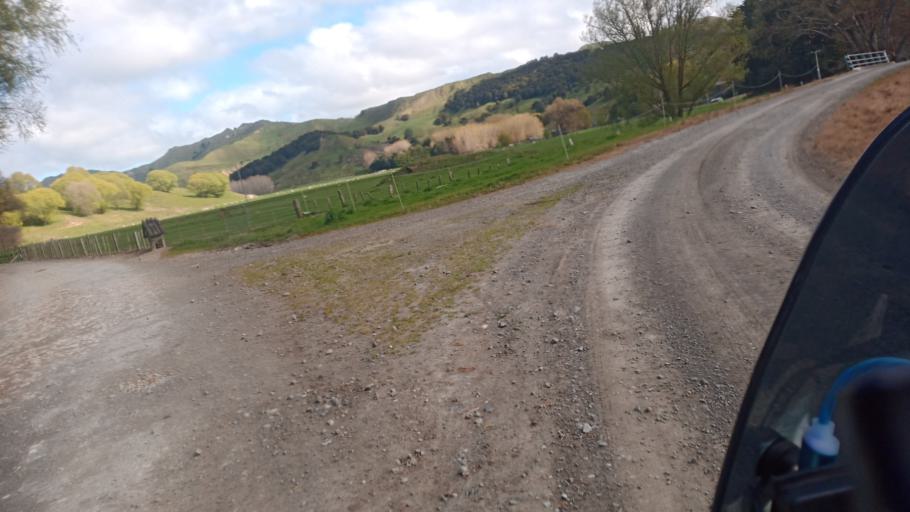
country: NZ
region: Gisborne
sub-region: Gisborne District
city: Gisborne
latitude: -38.3864
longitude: 178.2625
